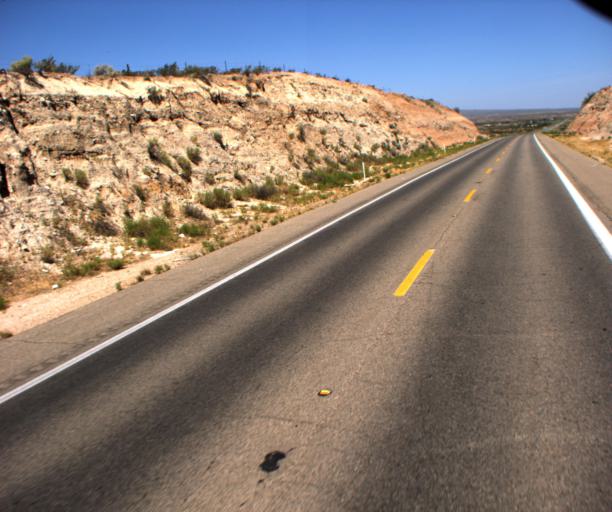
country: US
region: Arizona
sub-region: Graham County
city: Bylas
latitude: 33.0786
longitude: -110.0386
